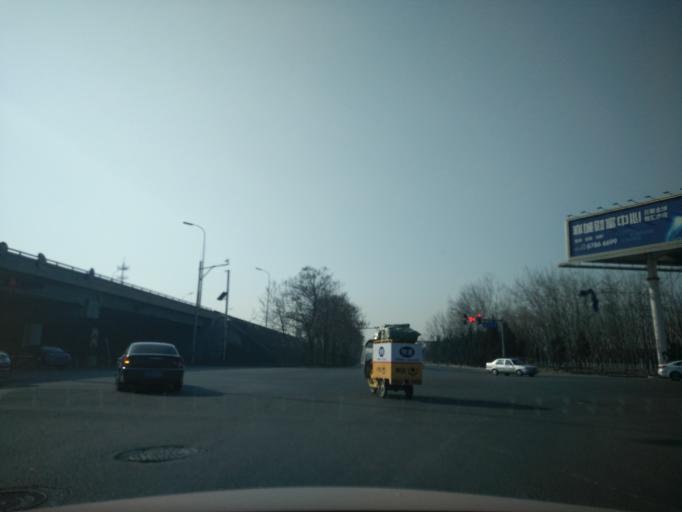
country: CN
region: Beijing
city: Jiugong
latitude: 39.8142
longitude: 116.4860
